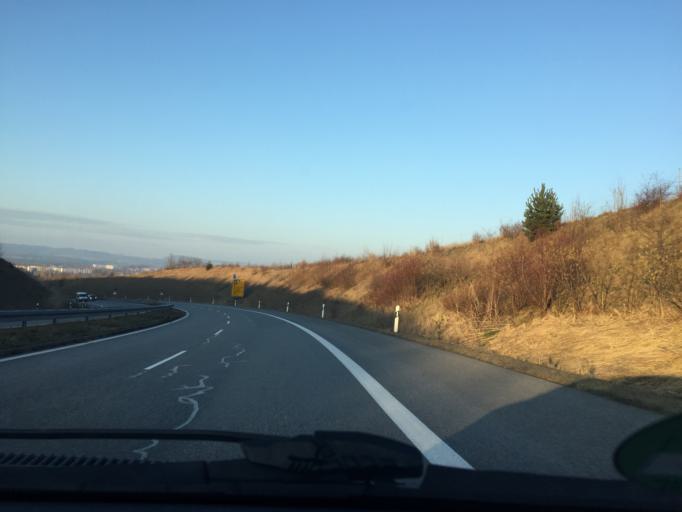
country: DE
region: Saxony
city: Pirna
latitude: 50.9489
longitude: 13.9227
